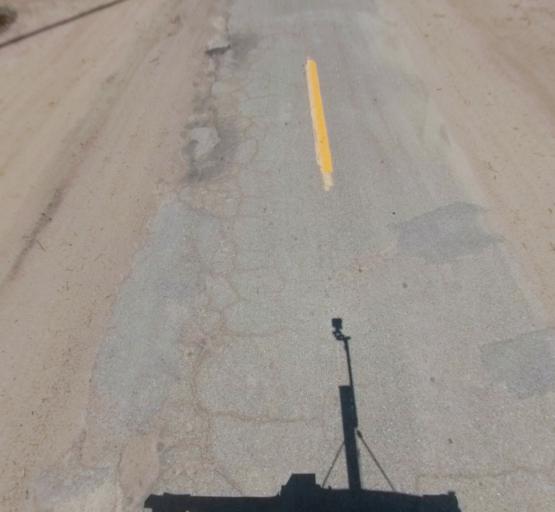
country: US
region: California
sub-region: Madera County
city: Chowchilla
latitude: 37.0982
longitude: -120.3996
